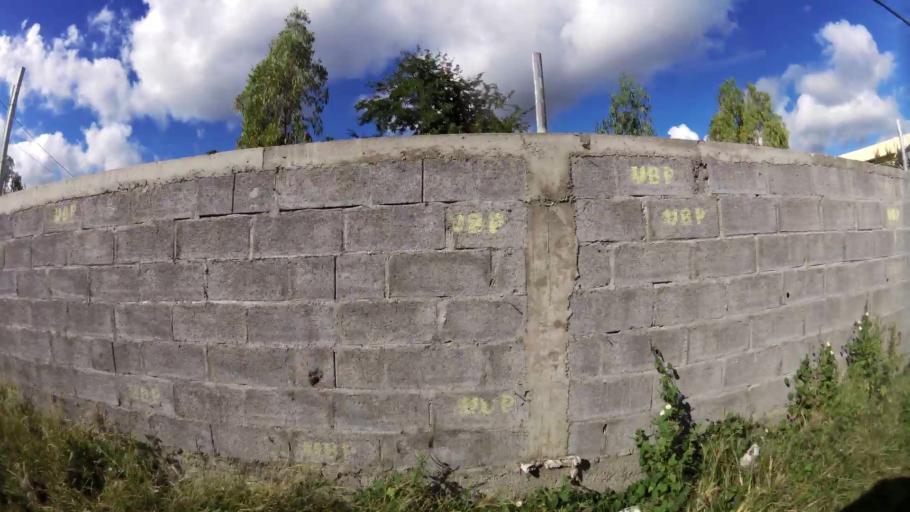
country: MU
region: Pamplemousses
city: Le Hochet
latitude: -20.1487
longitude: 57.5139
